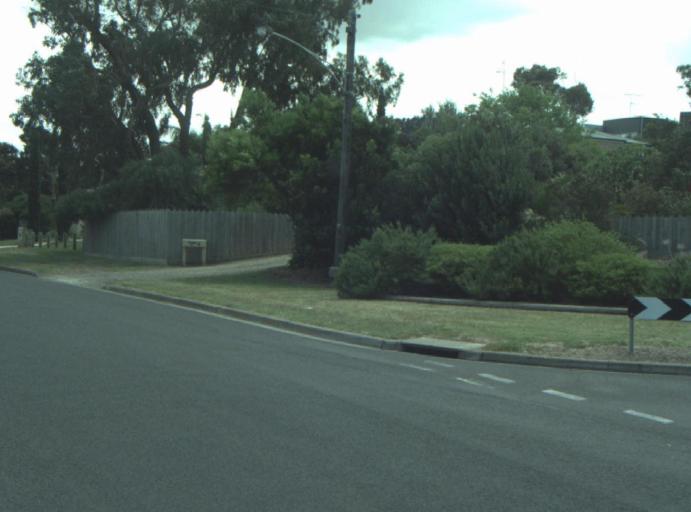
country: AU
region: Victoria
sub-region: Greater Geelong
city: Leopold
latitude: -38.2644
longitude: 144.5140
